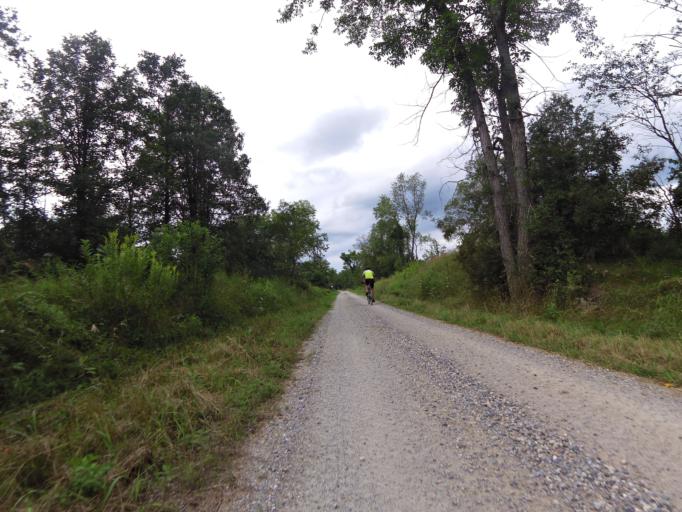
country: CA
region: Ontario
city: Perth
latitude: 44.8211
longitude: -76.5498
